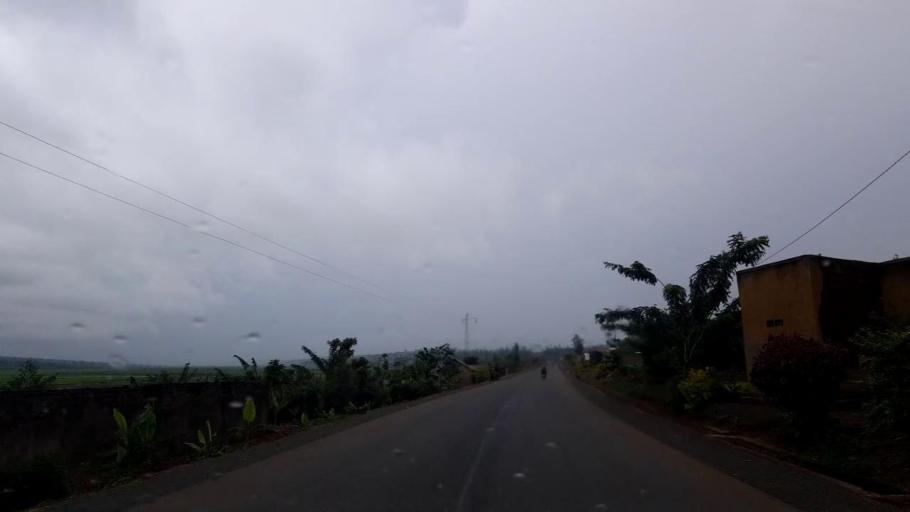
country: RW
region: Northern Province
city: Byumba
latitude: -1.4185
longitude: 30.2783
